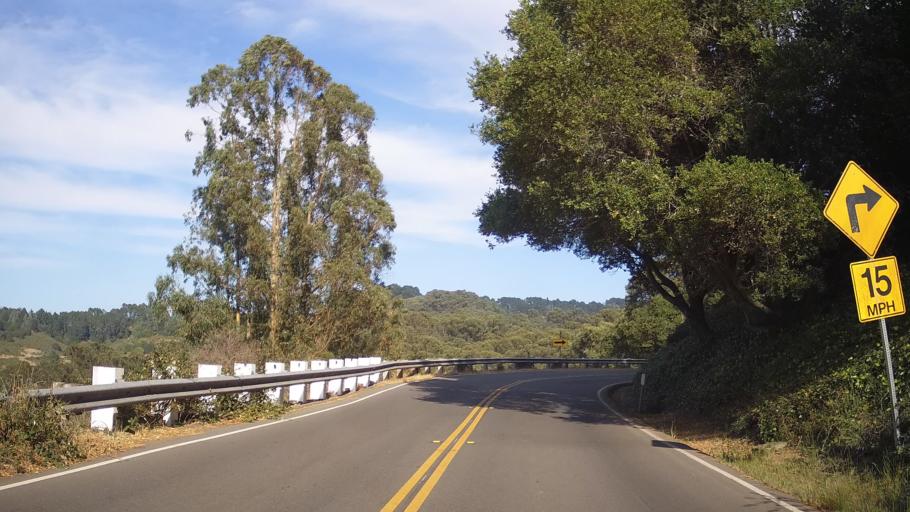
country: US
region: California
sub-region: Contra Costa County
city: Kensington
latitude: 37.9015
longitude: -122.2619
